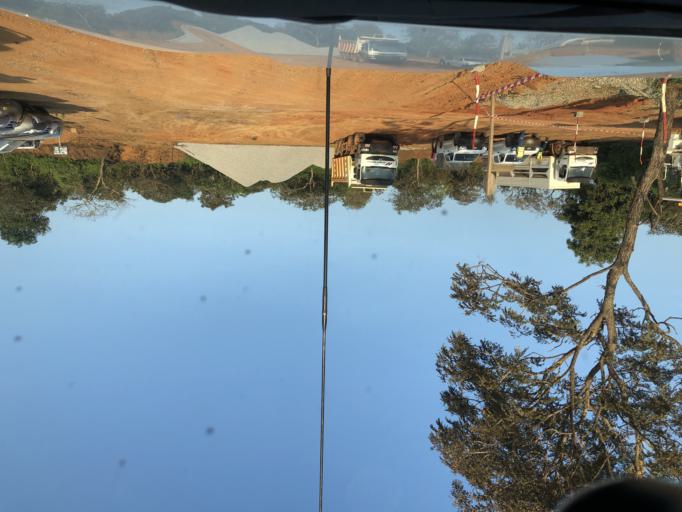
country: CF
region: Nana-Mambere
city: Bouar
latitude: 5.8941
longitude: 15.7614
